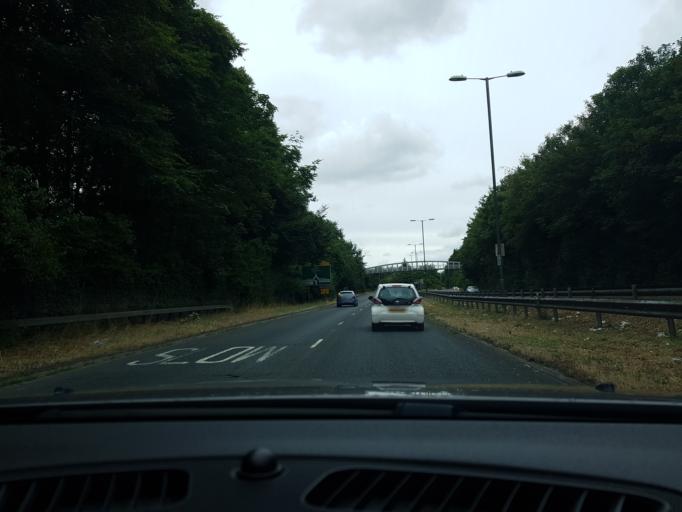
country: GB
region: England
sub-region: Hampshire
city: Basingstoke
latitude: 51.2768
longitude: -1.1225
